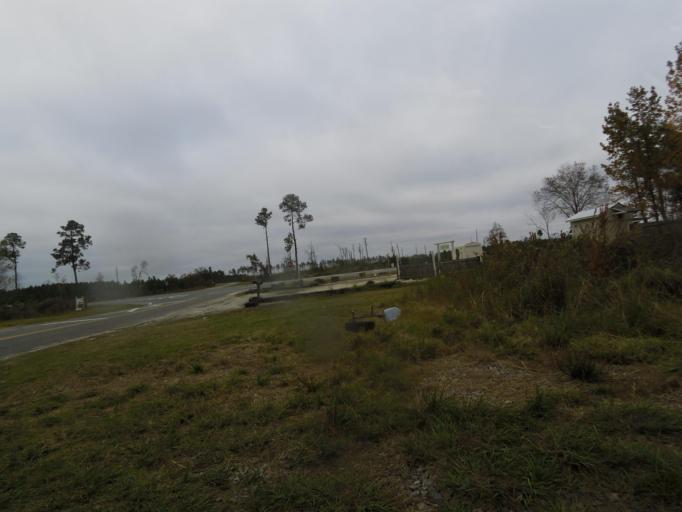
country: US
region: Georgia
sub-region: Charlton County
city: Folkston
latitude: 30.9171
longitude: -82.0854
